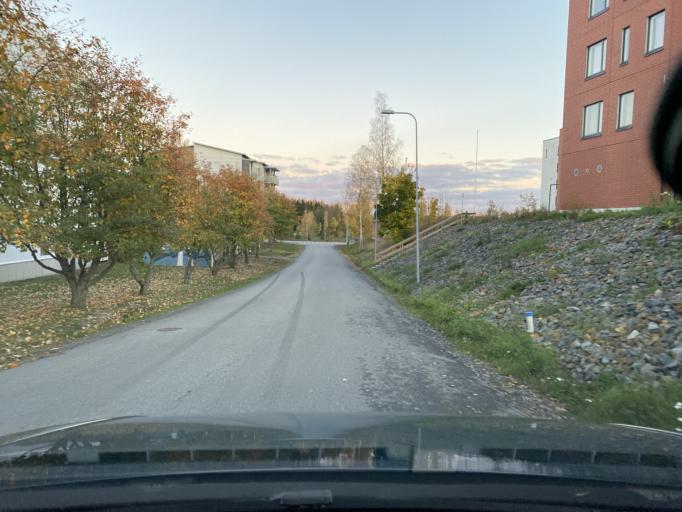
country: FI
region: Pirkanmaa
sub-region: Tampere
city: Lempaeaelae
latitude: 61.3166
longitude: 23.7580
